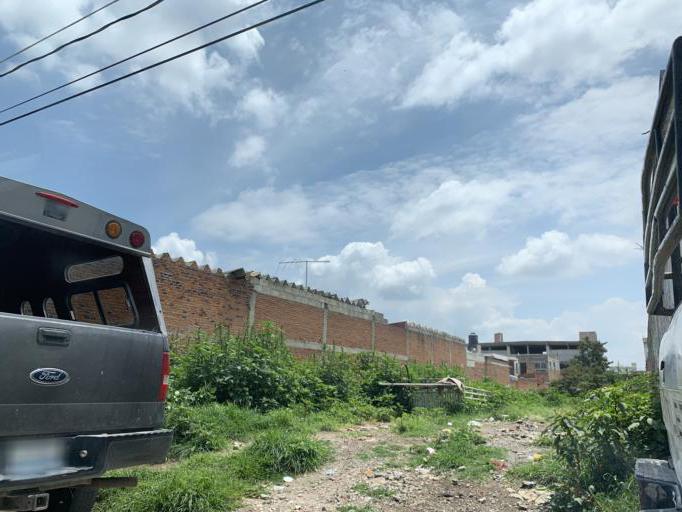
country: MX
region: Puebla
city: Huejotzingo
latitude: 19.1536
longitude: -98.4061
